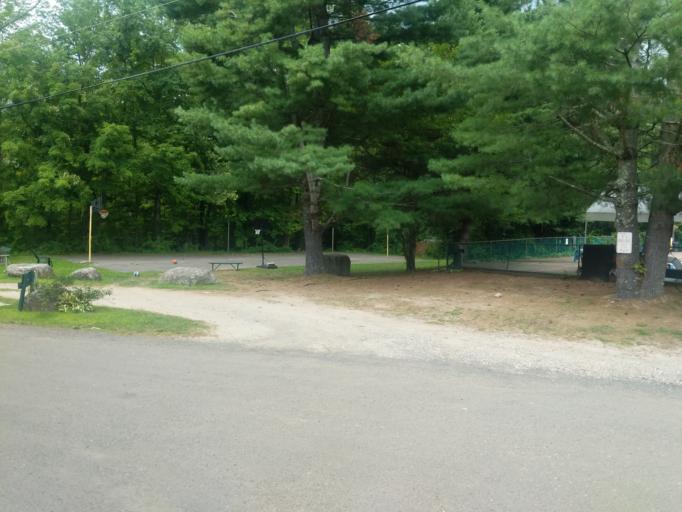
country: US
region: Connecticut
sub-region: Litchfield County
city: Winsted
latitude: 41.9397
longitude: -73.0382
